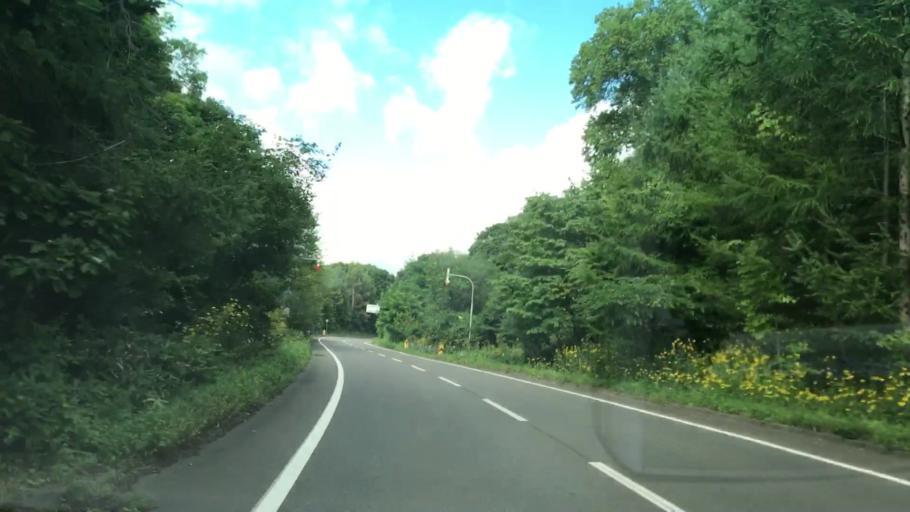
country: JP
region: Hokkaido
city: Muroran
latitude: 42.3698
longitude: 140.9578
